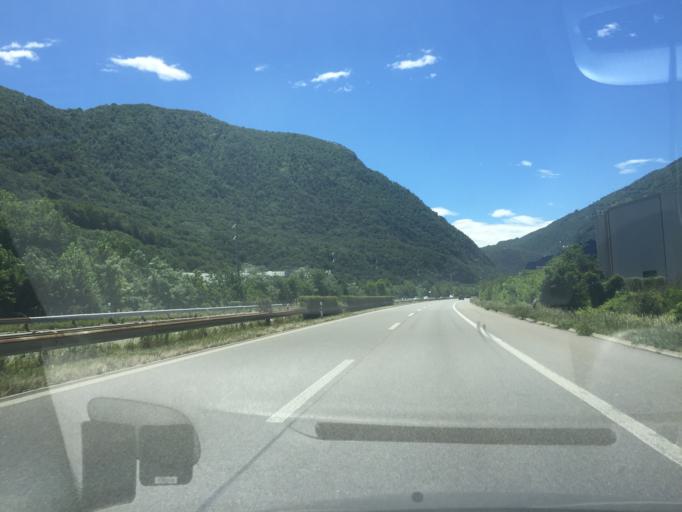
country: CH
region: Ticino
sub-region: Lugano District
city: Tesserete
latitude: 46.1028
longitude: 8.9311
